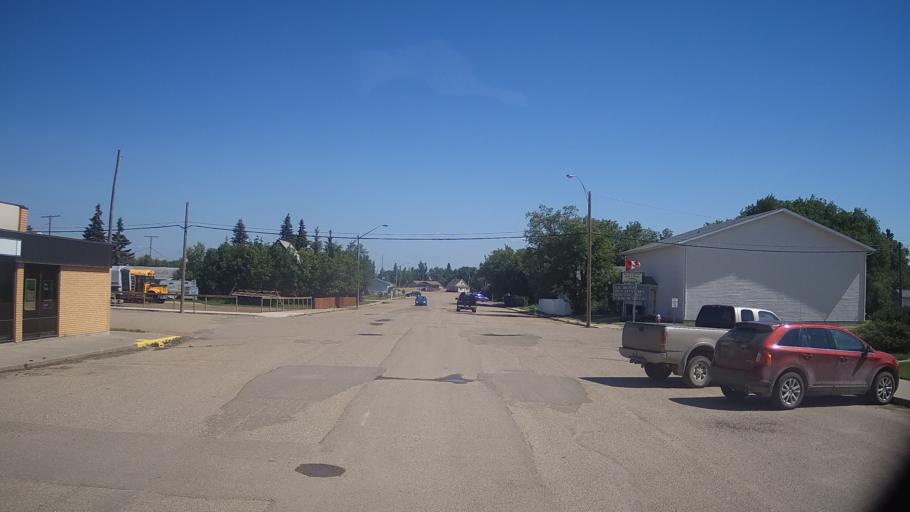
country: CA
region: Saskatchewan
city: Saskatoon
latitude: 51.8936
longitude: -106.0559
